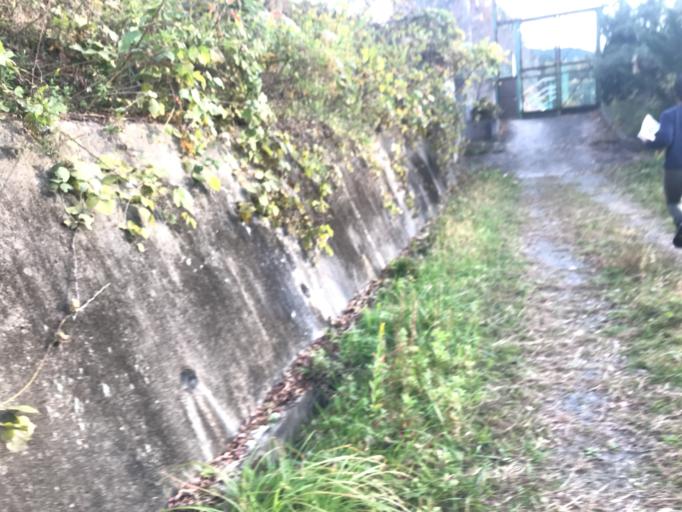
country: JP
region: Kyoto
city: Kameoka
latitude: 34.9921
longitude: 135.5539
